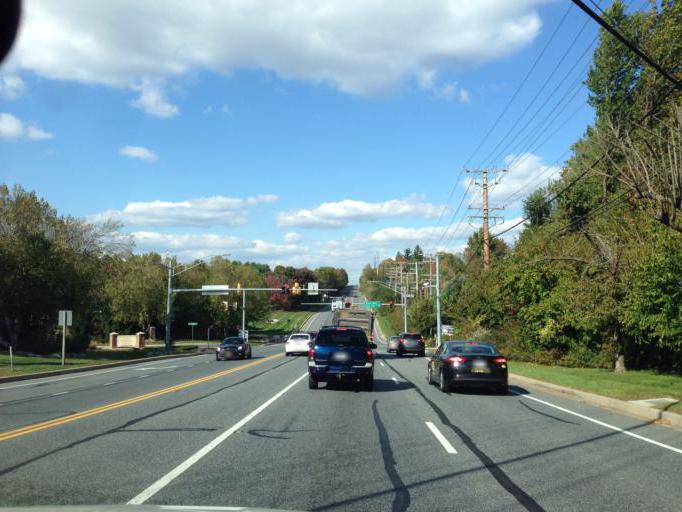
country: US
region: Maryland
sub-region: Baltimore County
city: Hunt Valley
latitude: 39.5128
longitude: -76.6417
